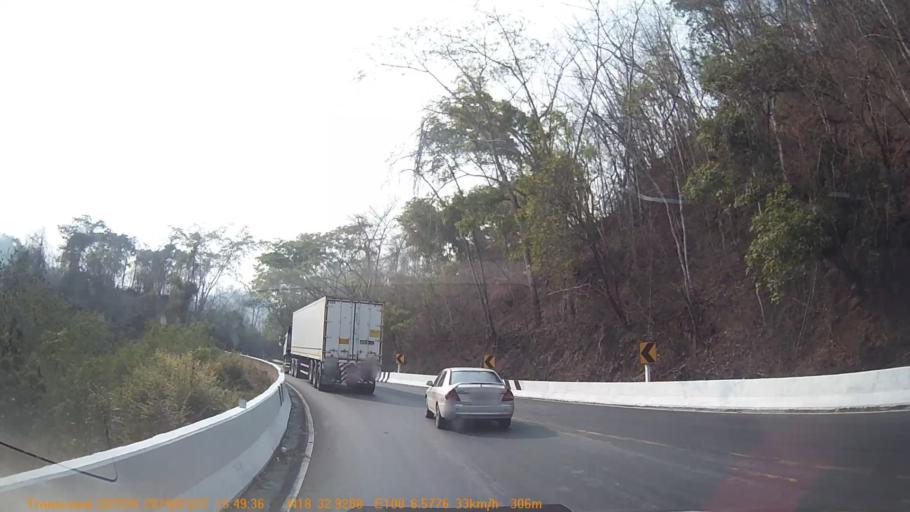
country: TH
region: Phrae
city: Song
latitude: 18.5489
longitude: 100.1095
